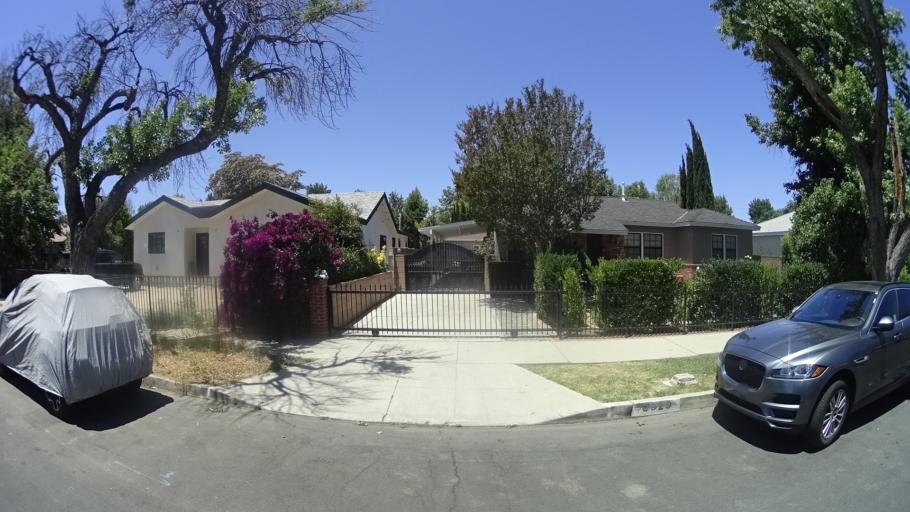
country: US
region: California
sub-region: Los Angeles County
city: Northridge
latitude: 34.1965
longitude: -118.5164
